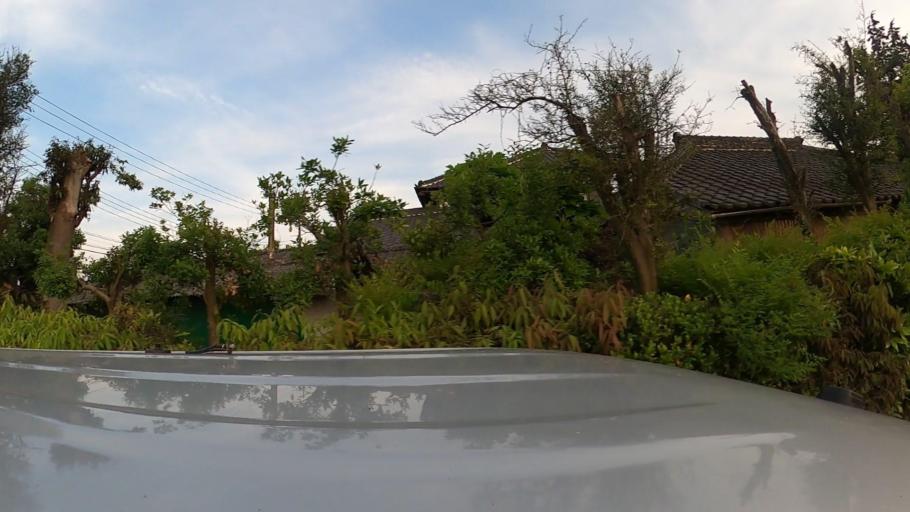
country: JP
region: Ibaraki
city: Ushiku
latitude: 36.0153
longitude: 140.1261
